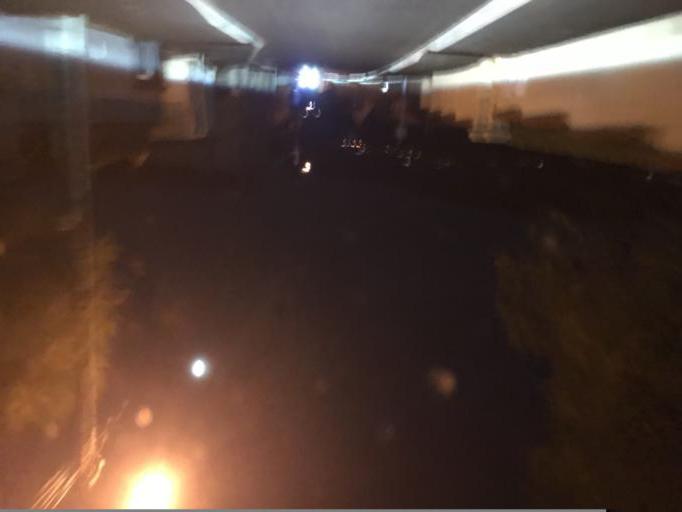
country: FR
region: Auvergne
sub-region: Departement du Puy-de-Dome
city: Thiers
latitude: 45.8596
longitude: 3.5327
